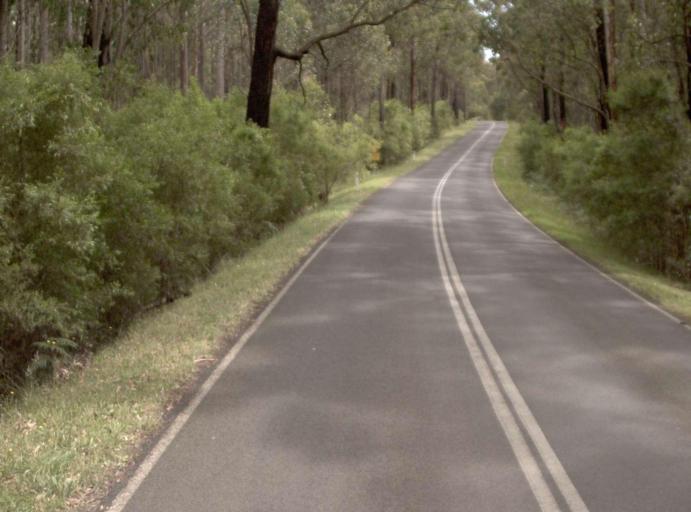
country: AU
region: Victoria
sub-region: Latrobe
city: Traralgon
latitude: -38.0329
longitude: 146.4197
